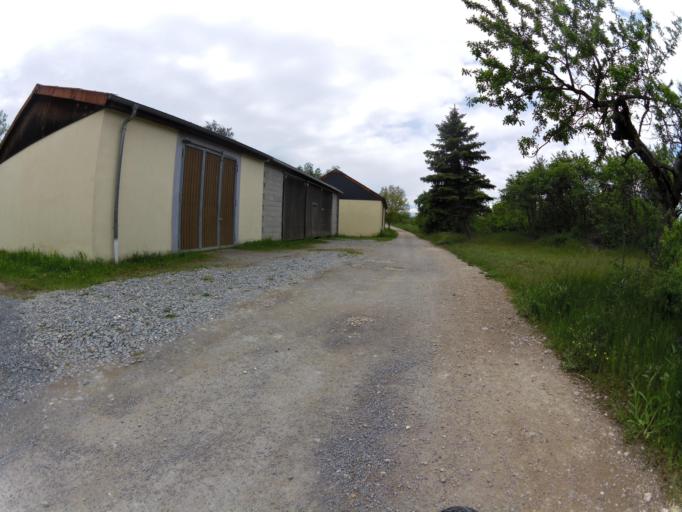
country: DE
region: Bavaria
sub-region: Regierungsbezirk Unterfranken
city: Sommerach
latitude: 49.8322
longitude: 10.2183
